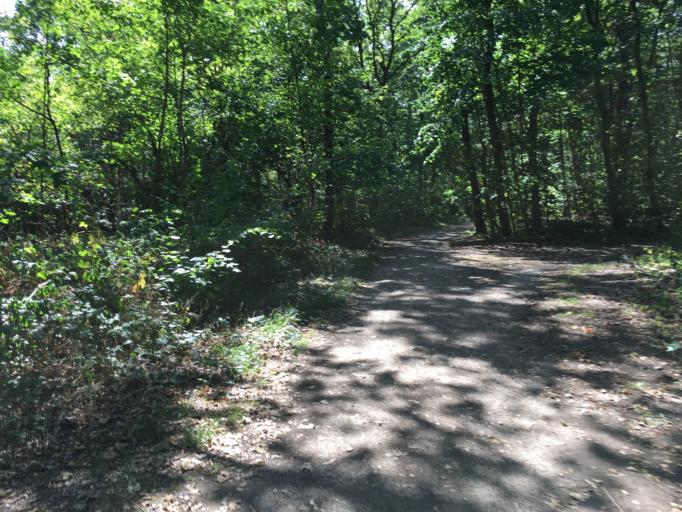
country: DE
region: North Rhine-Westphalia
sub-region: Regierungsbezirk Koln
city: Dueren
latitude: 50.7753
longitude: 6.5078
